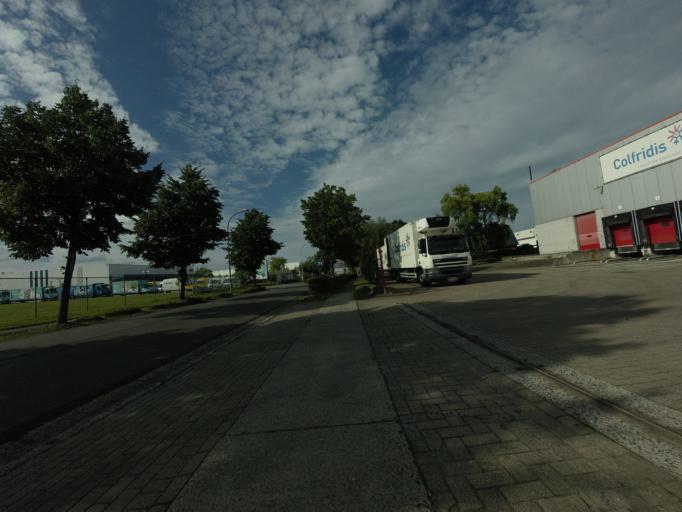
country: BE
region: Flanders
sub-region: Provincie Vlaams-Brabant
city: Londerzeel
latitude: 51.0122
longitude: 4.3211
